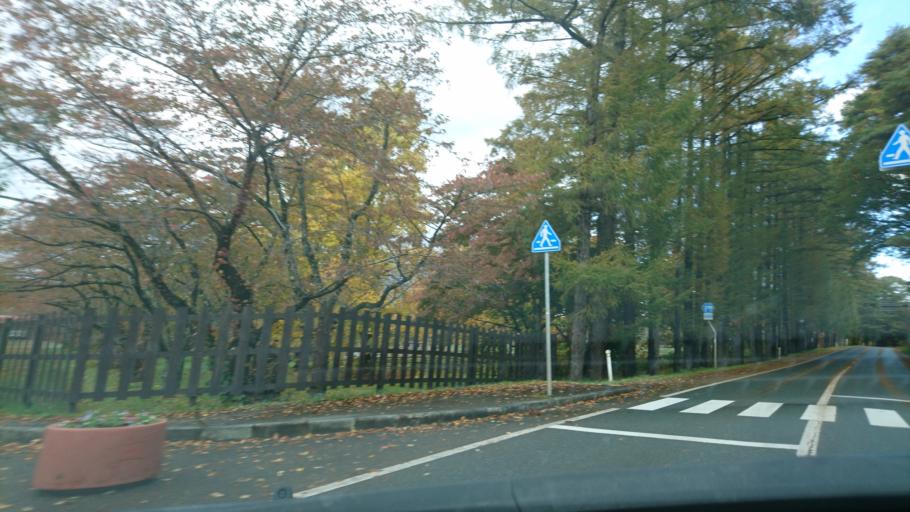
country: JP
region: Iwate
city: Shizukuishi
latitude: 39.7513
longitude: 141.0144
